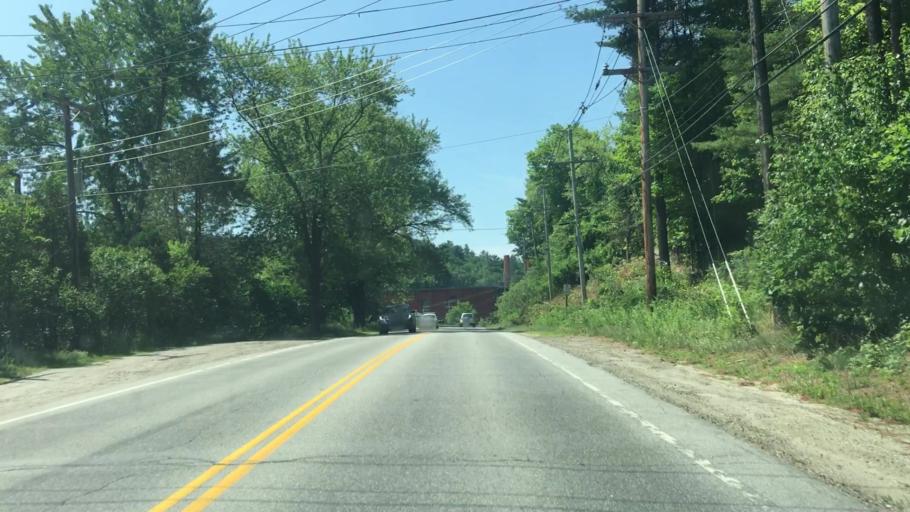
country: US
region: New Hampshire
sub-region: Sullivan County
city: Newport
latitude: 43.3684
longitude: -72.1627
